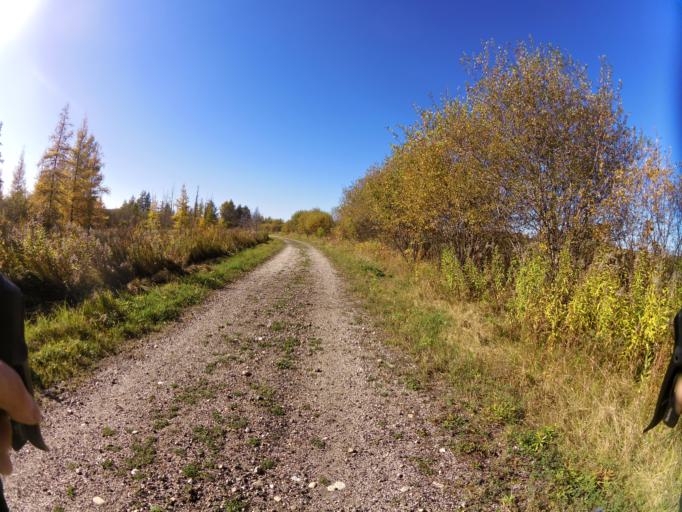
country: CA
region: Quebec
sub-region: Outaouais
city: Wakefield
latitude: 45.8663
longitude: -76.0174
